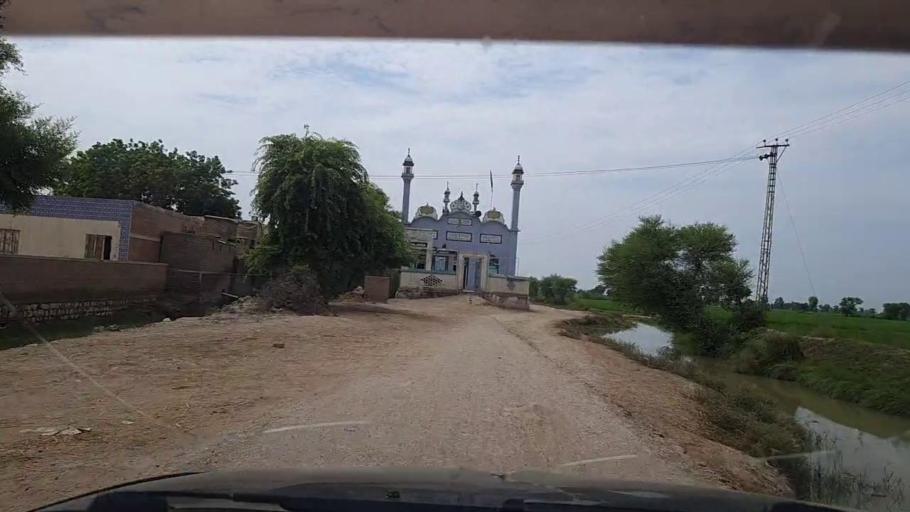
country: PK
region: Sindh
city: Thul
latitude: 28.2437
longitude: 68.7325
